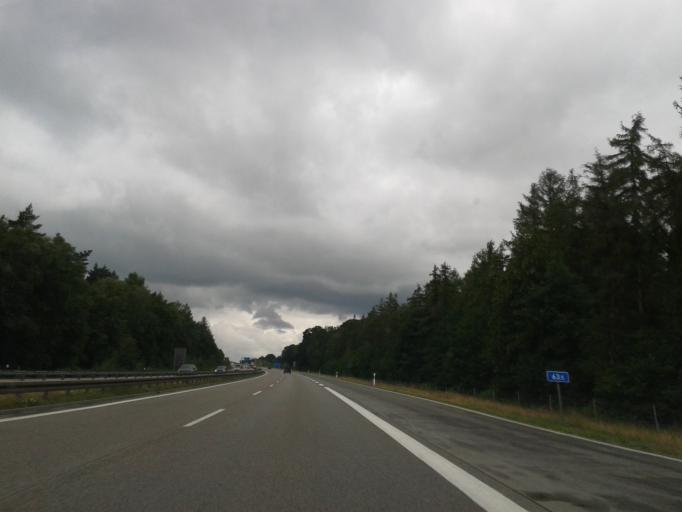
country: DE
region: Saxony
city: Naunhof
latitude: 51.3057
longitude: 12.5961
